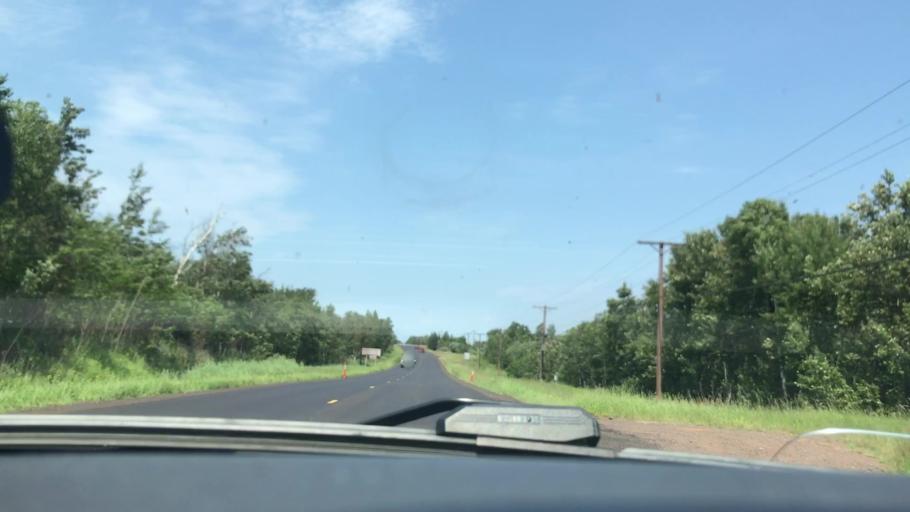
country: US
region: Minnesota
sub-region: Lake County
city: Silver Bay
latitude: 47.2771
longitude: -91.2735
